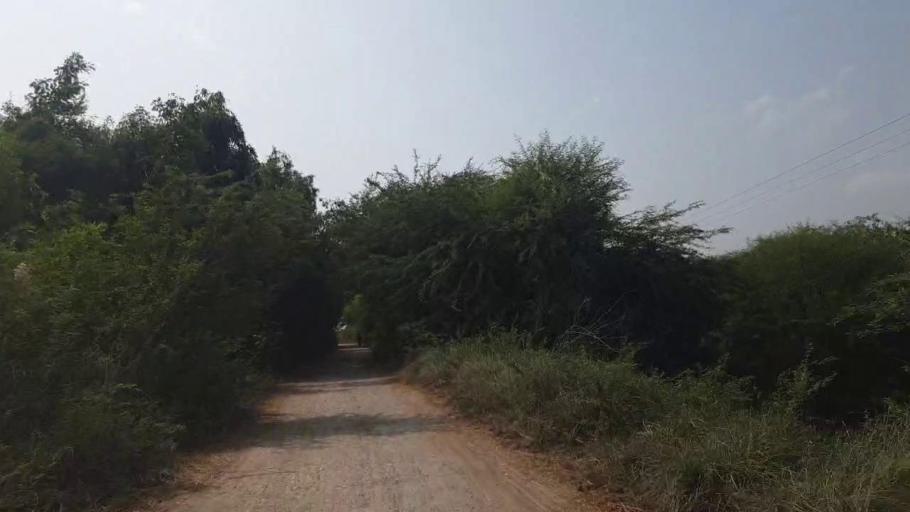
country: PK
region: Sindh
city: Badin
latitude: 24.7554
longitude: 68.7525
